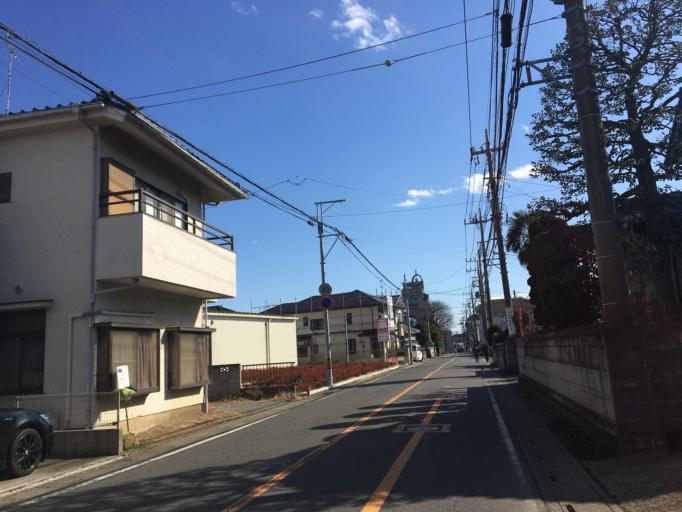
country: JP
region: Saitama
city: Oi
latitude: 35.8581
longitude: 139.5125
